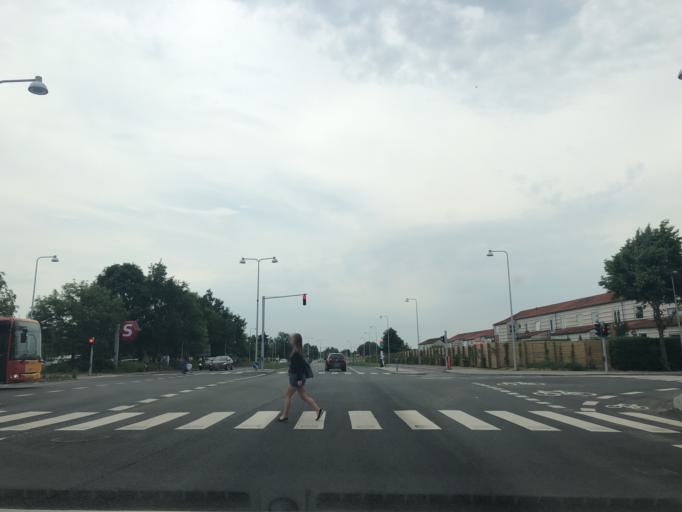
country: DK
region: Zealand
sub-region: Koge Kommune
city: Koge
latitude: 55.4804
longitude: 12.1729
